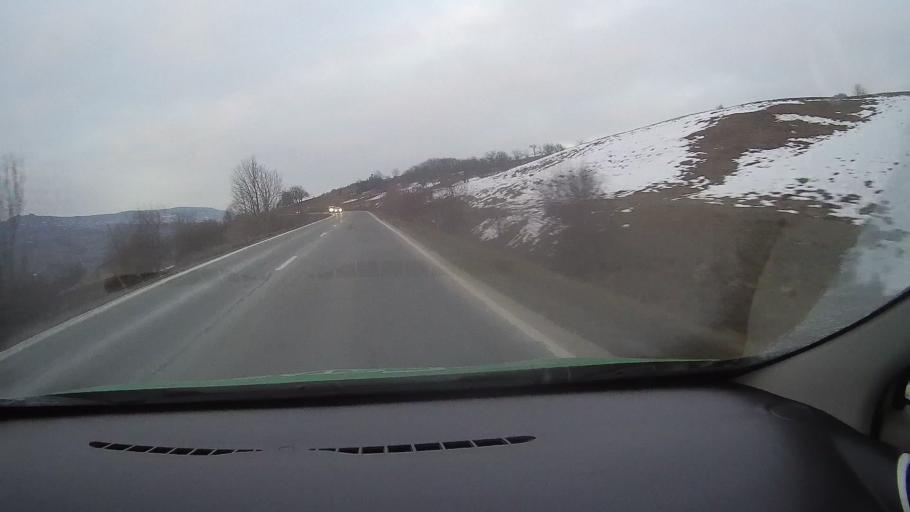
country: RO
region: Harghita
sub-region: Comuna Lupeni
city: Lupeni
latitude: 46.3570
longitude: 25.2452
